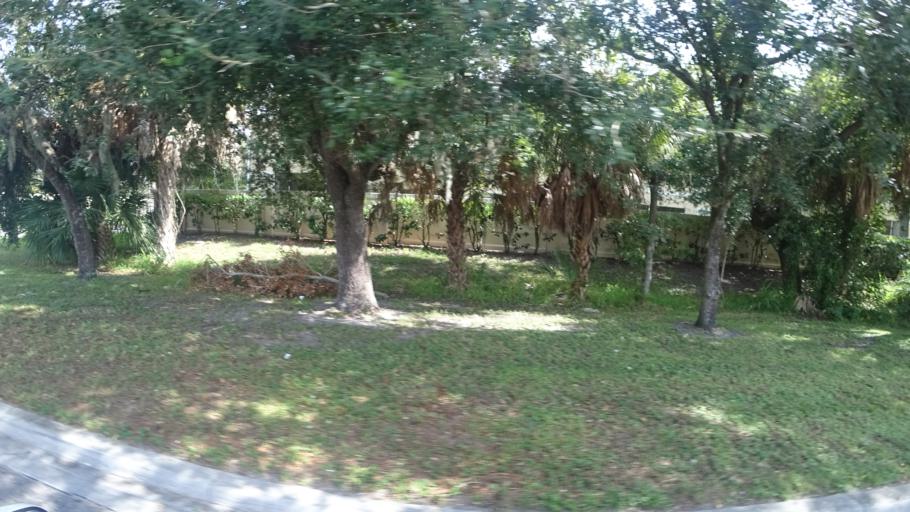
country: US
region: Florida
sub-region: Sarasota County
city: Desoto Lakes
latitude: 27.3878
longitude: -82.5016
